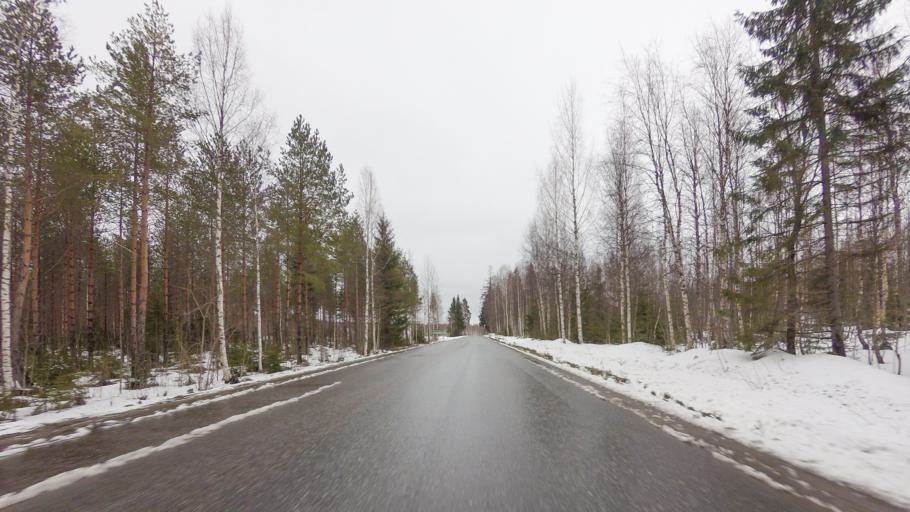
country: FI
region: Southern Savonia
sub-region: Savonlinna
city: Savonlinna
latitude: 61.9189
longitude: 28.8996
